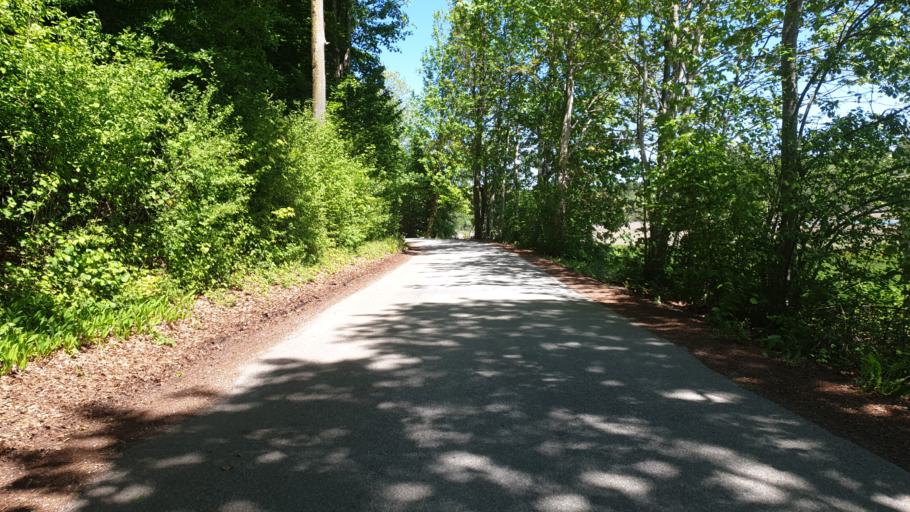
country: DE
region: Bavaria
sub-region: Upper Bavaria
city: Seeshaupt
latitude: 47.7938
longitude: 11.2937
